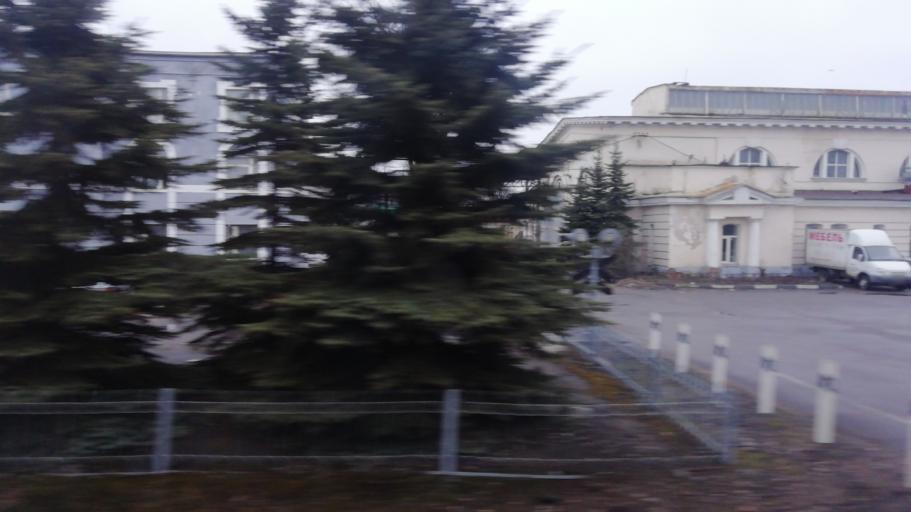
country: RU
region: St.-Petersburg
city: Kupchino
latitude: 59.8874
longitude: 30.3452
